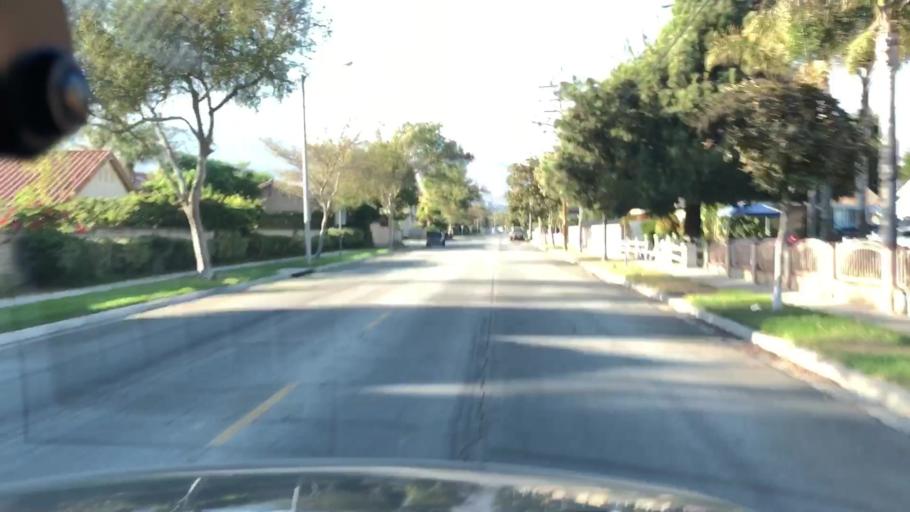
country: US
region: California
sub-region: Ventura County
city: Fillmore
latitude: 34.3990
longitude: -118.9280
